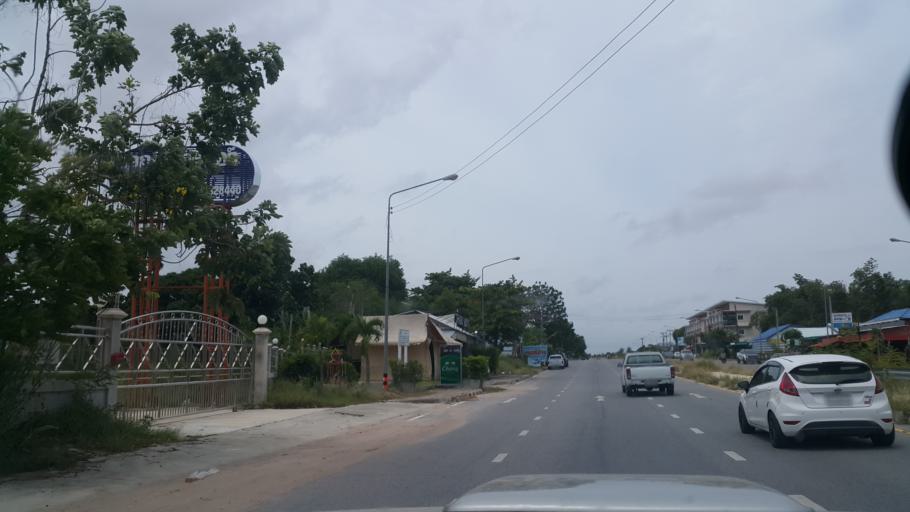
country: TH
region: Rayong
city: Ban Chang
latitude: 12.7152
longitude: 101.0608
